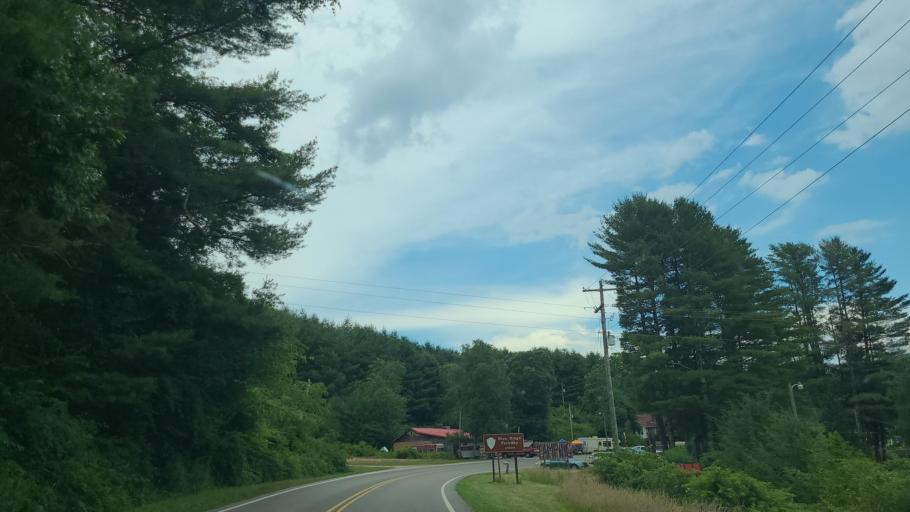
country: US
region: North Carolina
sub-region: Alleghany County
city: Sparta
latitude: 36.3946
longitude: -81.2483
